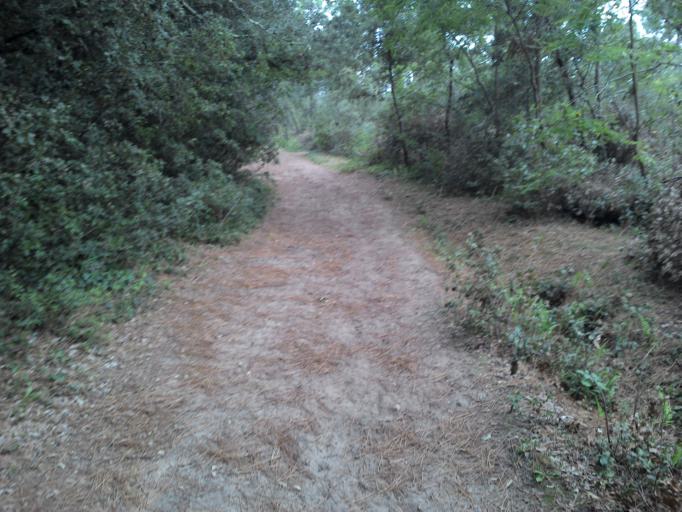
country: FR
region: Poitou-Charentes
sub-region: Departement de la Charente-Maritime
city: Saint-Denis-d'Oleron
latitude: 45.9965
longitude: -1.3821
